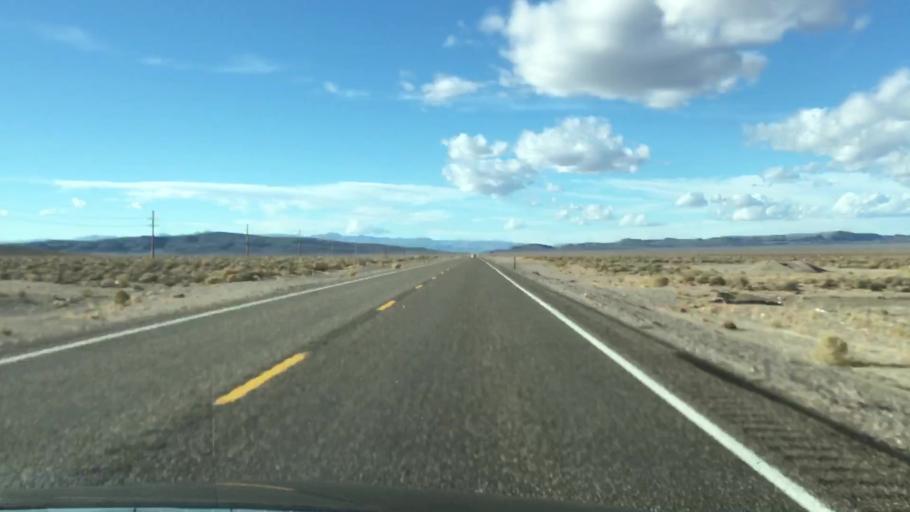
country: US
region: Nevada
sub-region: Nye County
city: Beatty
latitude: 37.1305
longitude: -116.8411
